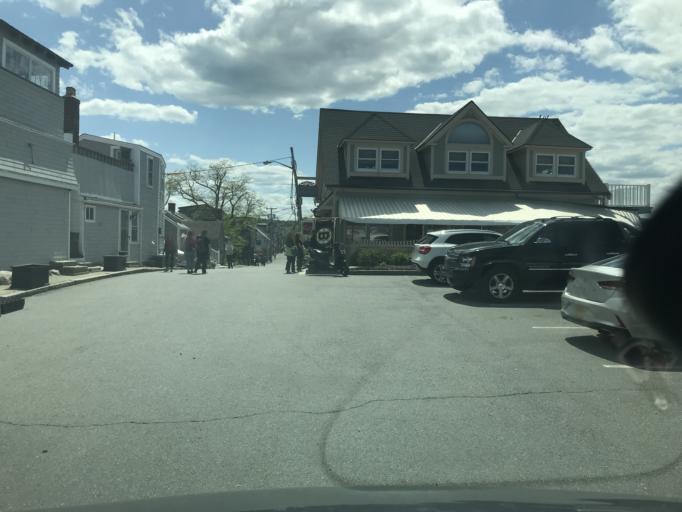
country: US
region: Massachusetts
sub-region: Essex County
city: Rockport
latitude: 42.6609
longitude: -70.6142
